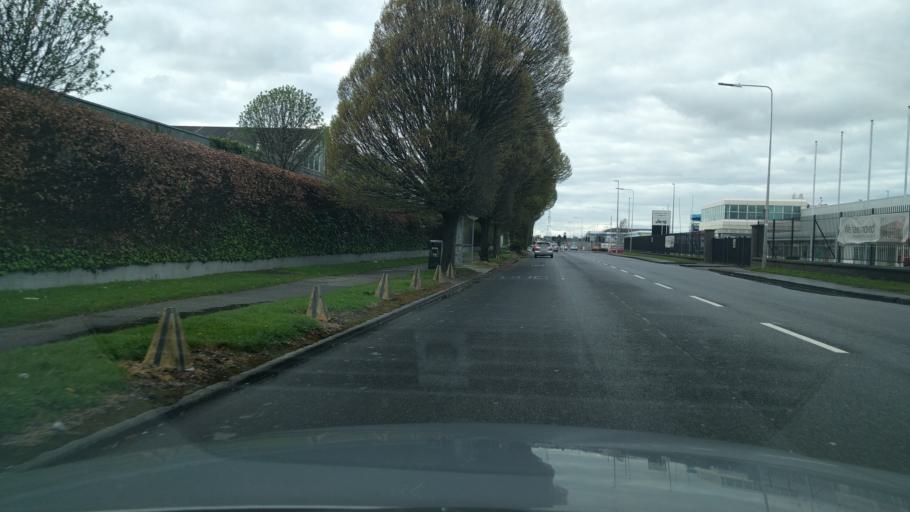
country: IE
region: Leinster
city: Crumlin
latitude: 53.3254
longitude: -6.3418
